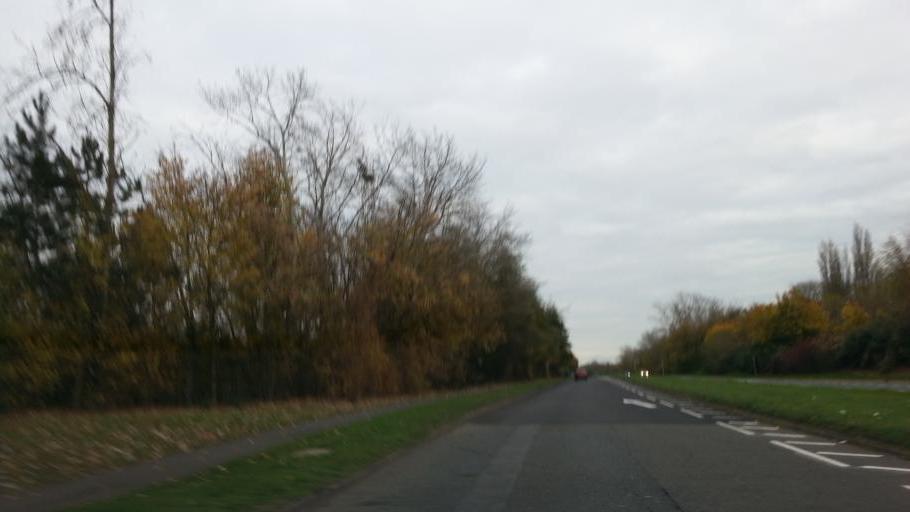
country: GB
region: England
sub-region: Northamptonshire
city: Corby
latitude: 52.4925
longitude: -0.6687
